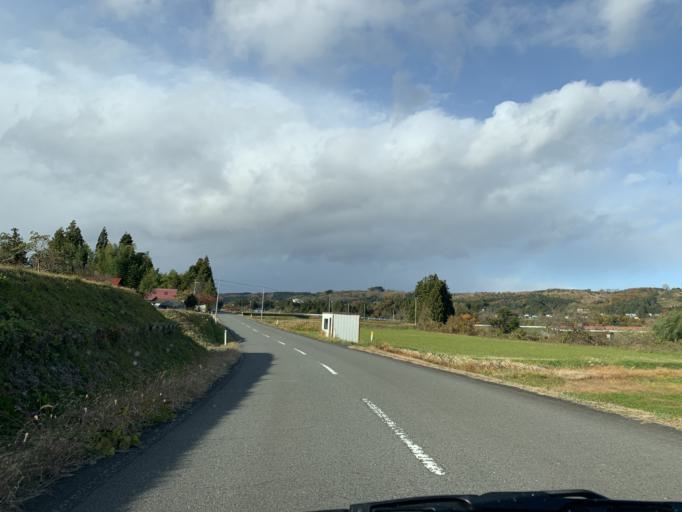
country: JP
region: Iwate
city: Ichinoseki
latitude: 39.0223
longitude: 141.0747
